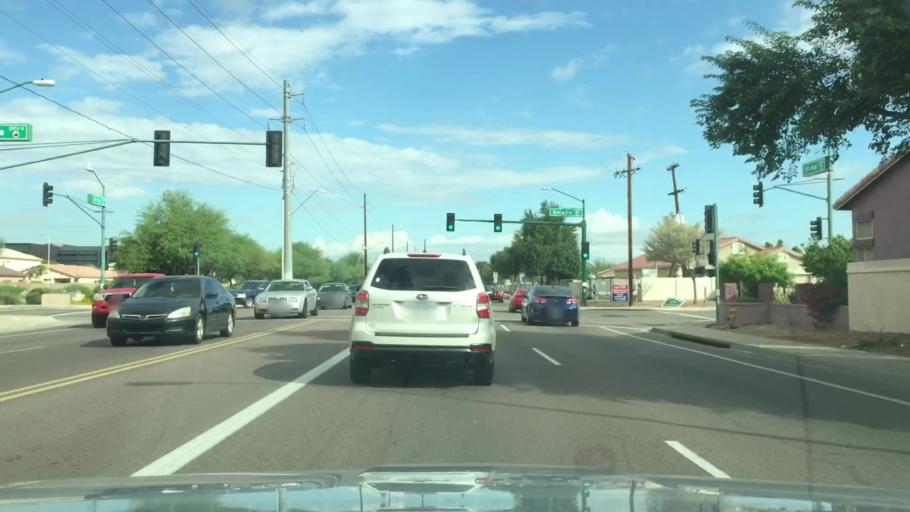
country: US
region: Arizona
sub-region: Maricopa County
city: Tolleson
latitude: 33.4718
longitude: -112.2552
